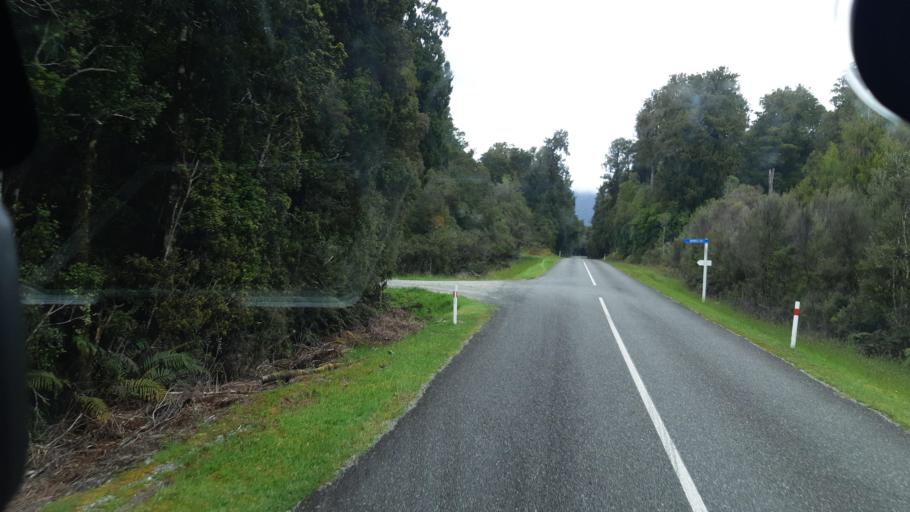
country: NZ
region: West Coast
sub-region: Westland District
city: Hokitika
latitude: -42.7845
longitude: 171.1177
